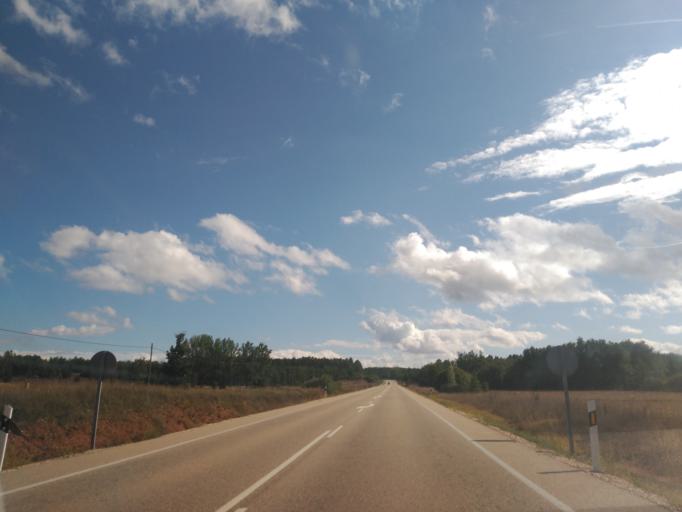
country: ES
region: Castille and Leon
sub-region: Provincia de Burgos
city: Hacinas
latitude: 41.9522
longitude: -3.2916
